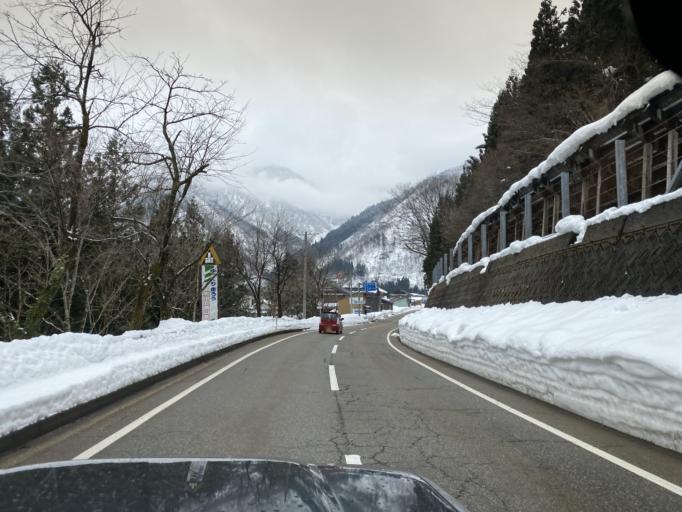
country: JP
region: Toyama
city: Fukumitsu
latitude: 36.4050
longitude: 136.9248
